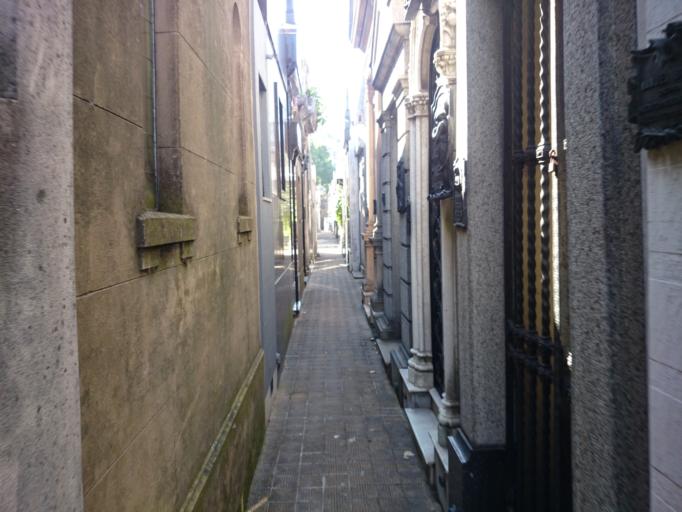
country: AR
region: Buenos Aires F.D.
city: Retiro
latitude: -34.5869
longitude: -58.3931
